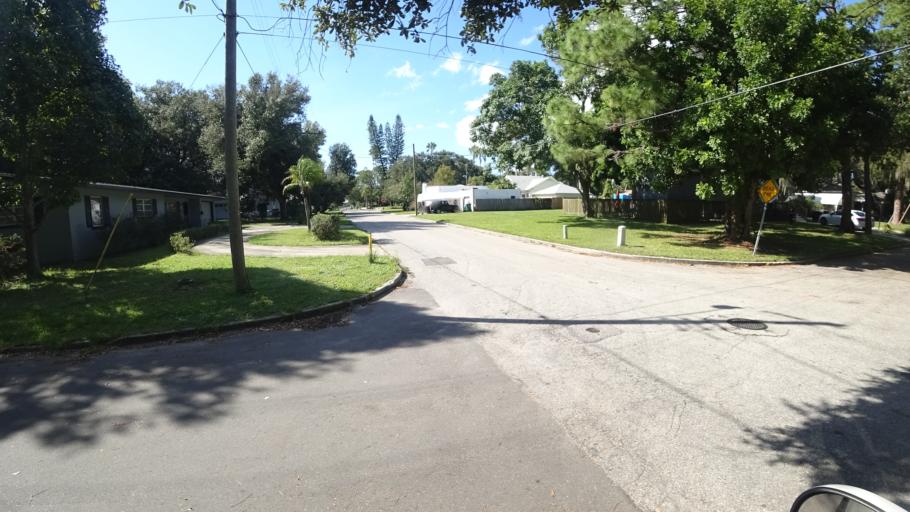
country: US
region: Florida
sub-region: Manatee County
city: Bradenton
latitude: 27.4872
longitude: -82.5826
